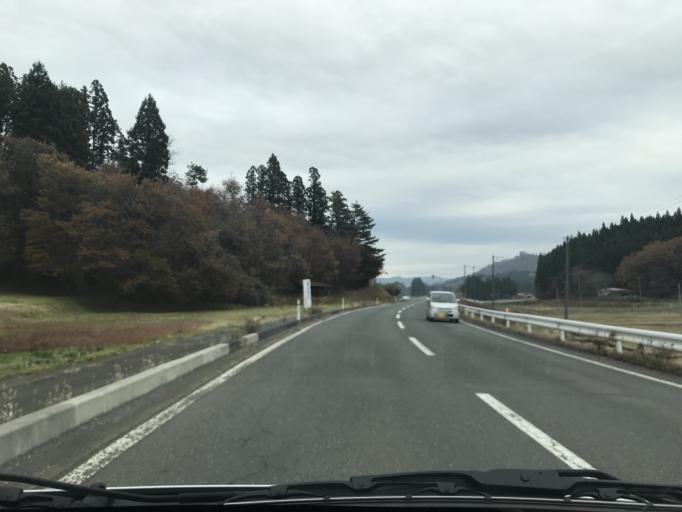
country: JP
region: Iwate
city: Kitakami
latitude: 39.2961
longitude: 141.1810
